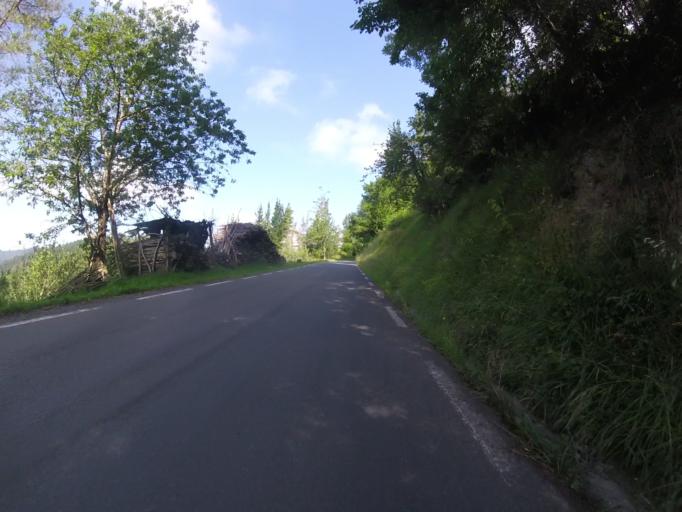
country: ES
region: Basque Country
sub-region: Provincia de Guipuzcoa
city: Beasain
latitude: 43.0776
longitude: -2.2236
